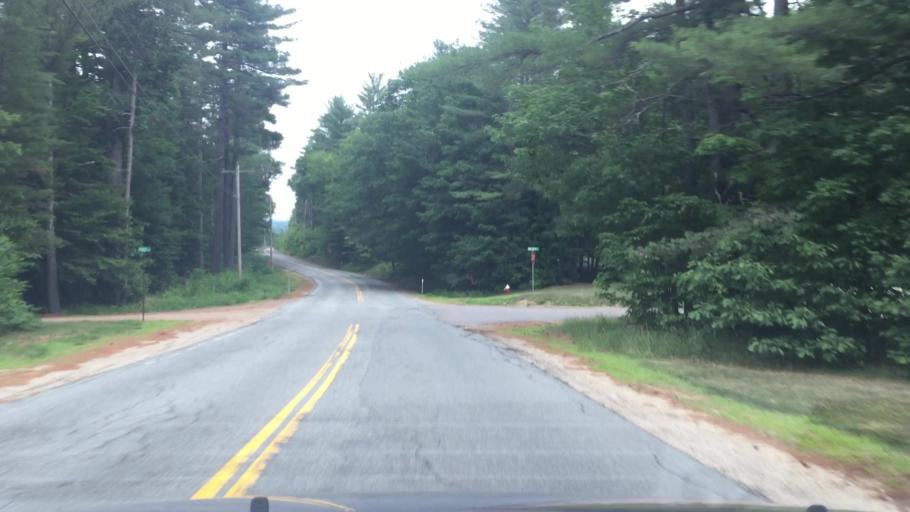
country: US
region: New Hampshire
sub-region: Carroll County
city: North Conway
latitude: 44.0938
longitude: -71.2006
